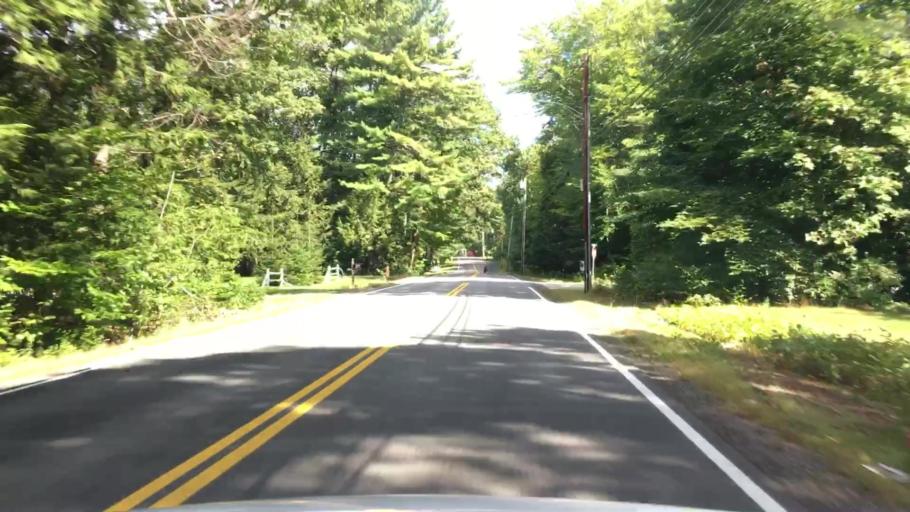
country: US
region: Maine
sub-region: Cumberland County
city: West Scarborough
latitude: 43.6068
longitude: -70.4137
